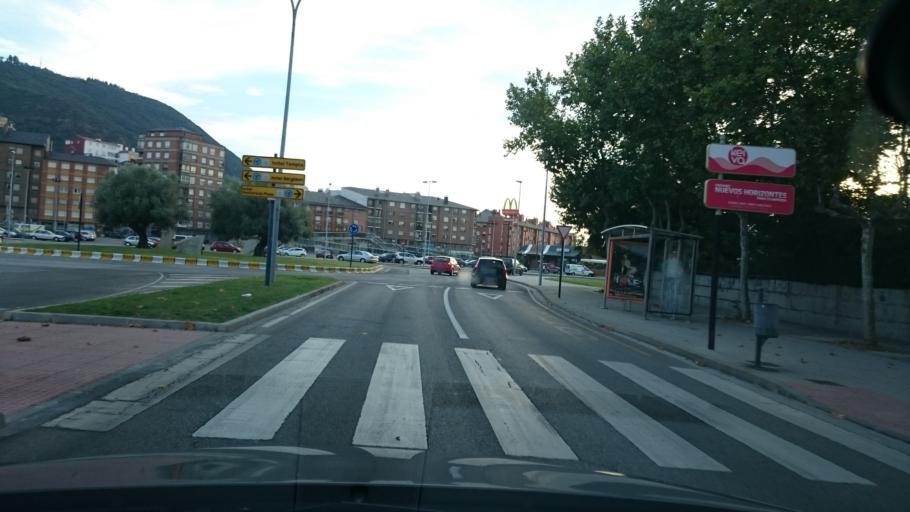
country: ES
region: Castille and Leon
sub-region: Provincia de Leon
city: Ponferrada
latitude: 42.5493
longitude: -6.6054
